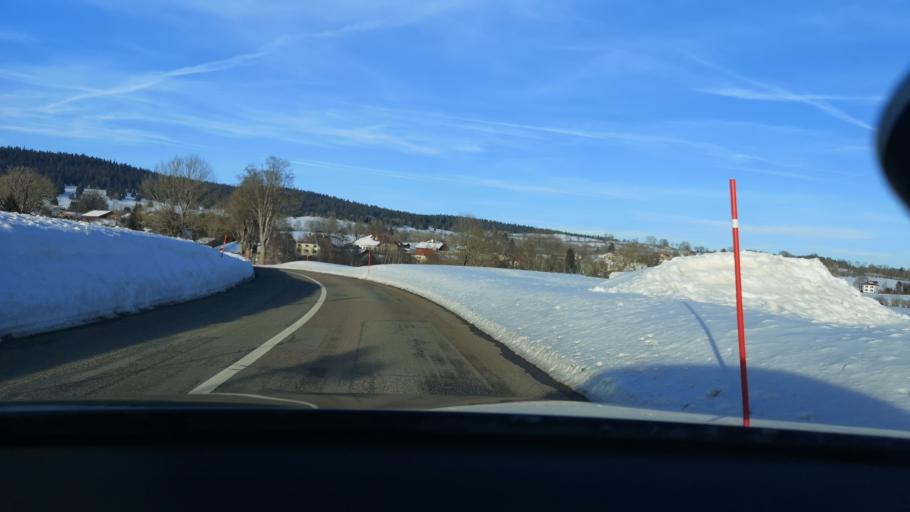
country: CH
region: Neuchatel
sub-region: Val-de-Travers District
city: Fleurier
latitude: 46.9129
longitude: 6.5090
